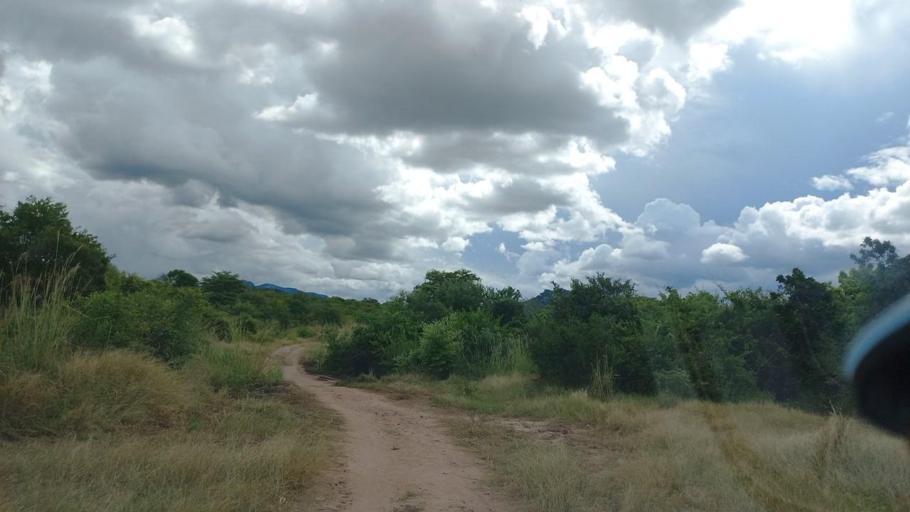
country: ZM
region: Lusaka
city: Luangwa
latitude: -15.6409
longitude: 30.3772
